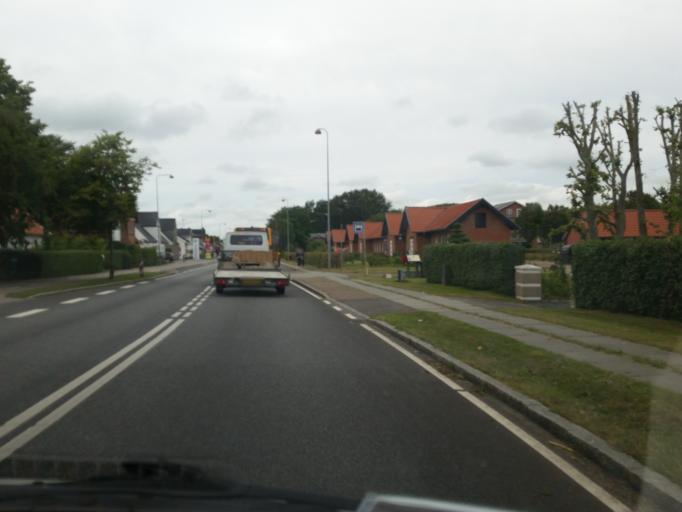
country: DK
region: South Denmark
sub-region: Esbjerg Kommune
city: Ribe
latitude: 55.2744
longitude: 8.7284
